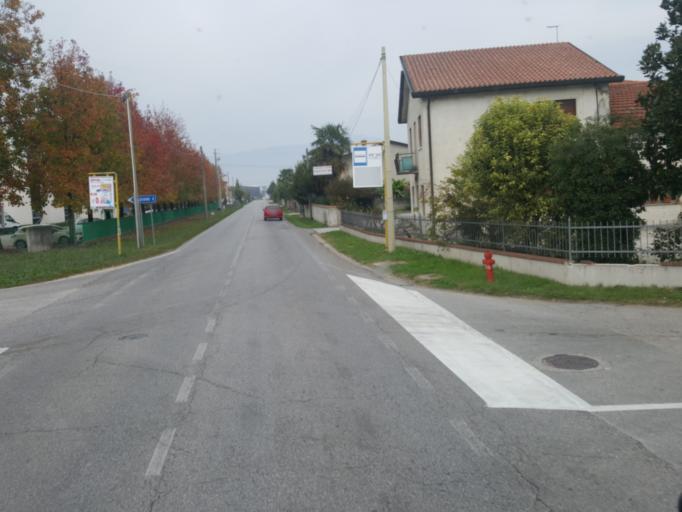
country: IT
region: Veneto
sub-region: Provincia di Treviso
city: Castello di Godego
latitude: 45.7026
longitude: 11.8733
